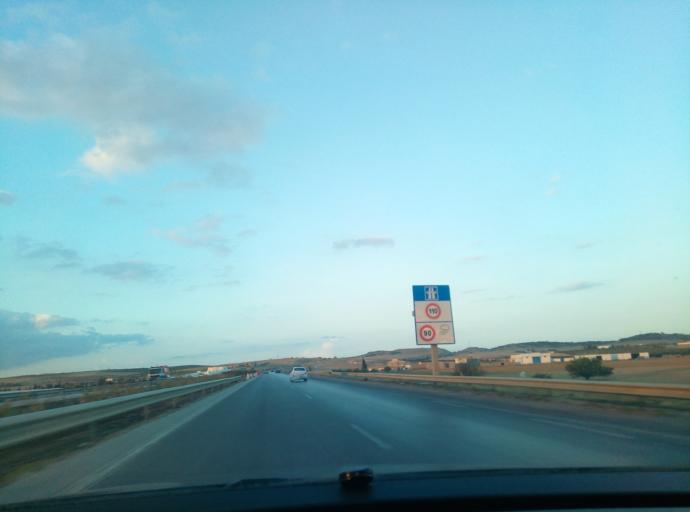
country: TN
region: Manouba
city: Manouba
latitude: 36.7451
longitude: 10.0353
